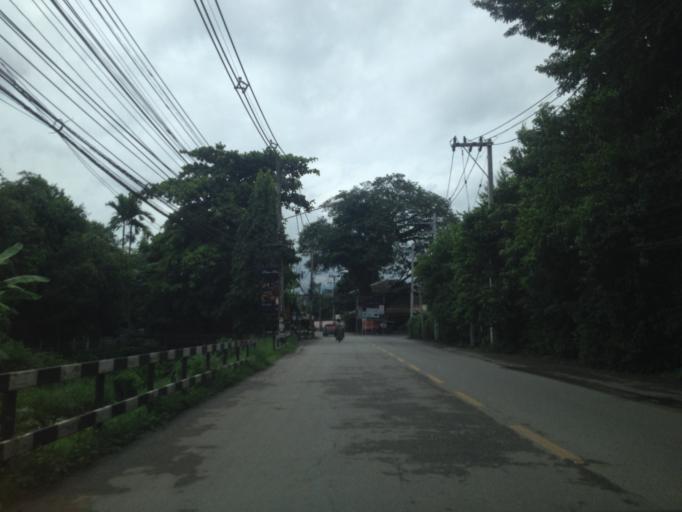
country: TH
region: Chiang Mai
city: Chiang Mai
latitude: 18.7749
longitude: 99.0080
